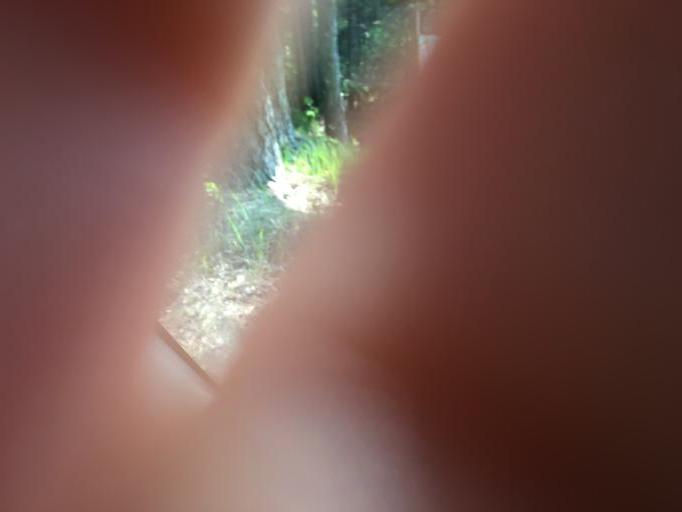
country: LV
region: Ventspils
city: Ventspils
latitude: 57.4701
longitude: 21.7722
